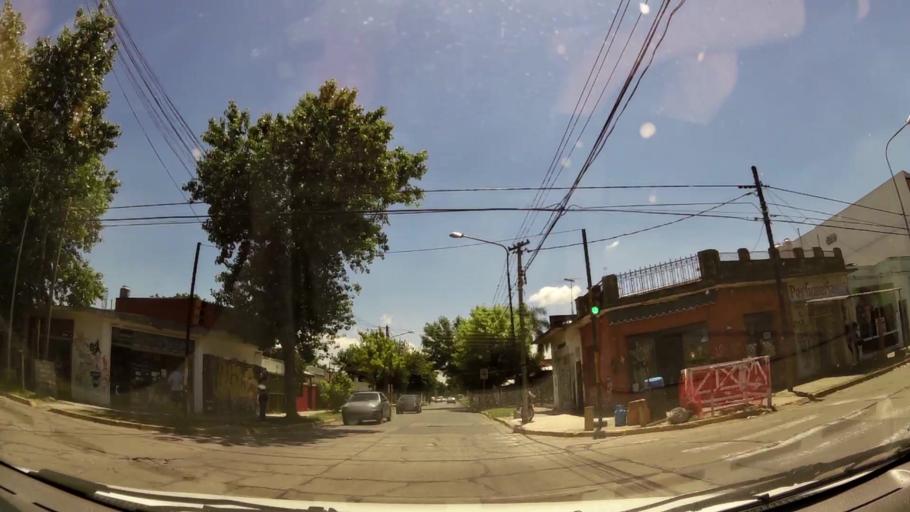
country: AR
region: Buenos Aires
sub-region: Partido de Merlo
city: Merlo
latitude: -34.6601
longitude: -58.7133
